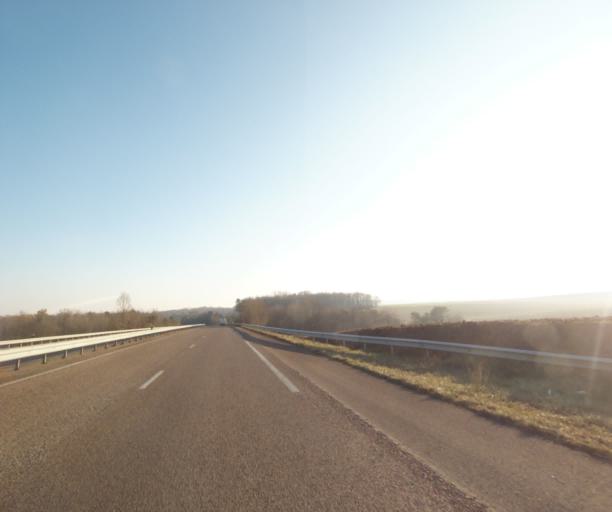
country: FR
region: Champagne-Ardenne
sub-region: Departement de la Haute-Marne
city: Chevillon
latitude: 48.5126
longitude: 5.0936
